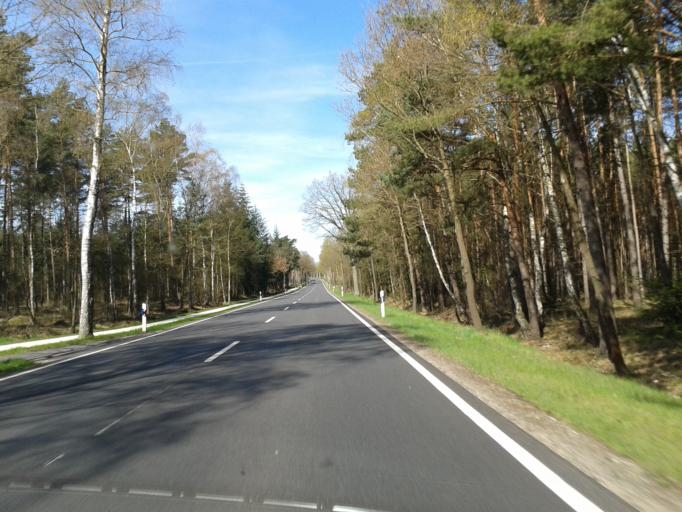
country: DE
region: Lower Saxony
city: Schnega
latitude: 52.9277
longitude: 10.8362
